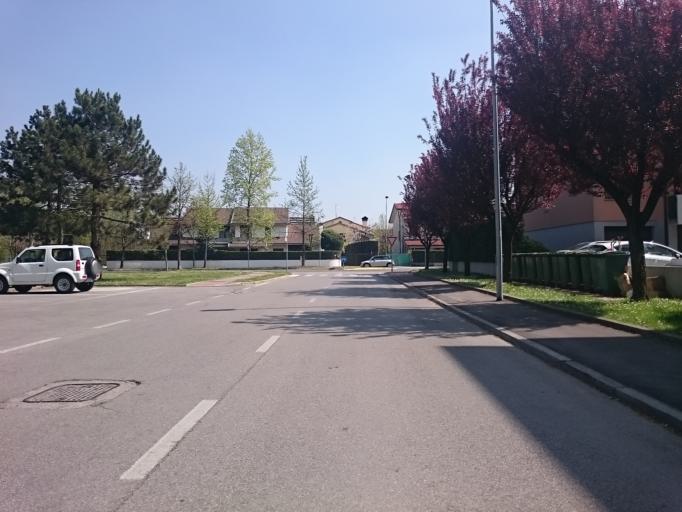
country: IT
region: Veneto
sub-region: Provincia di Padova
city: Caselle
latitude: 45.4160
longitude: 11.8143
